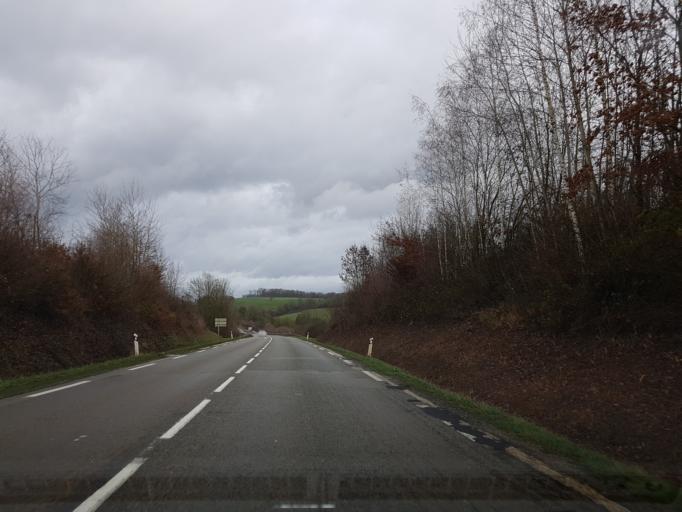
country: FR
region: Franche-Comte
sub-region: Departement de la Haute-Saone
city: Magny-Vernois
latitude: 47.6613
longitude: 6.3719
